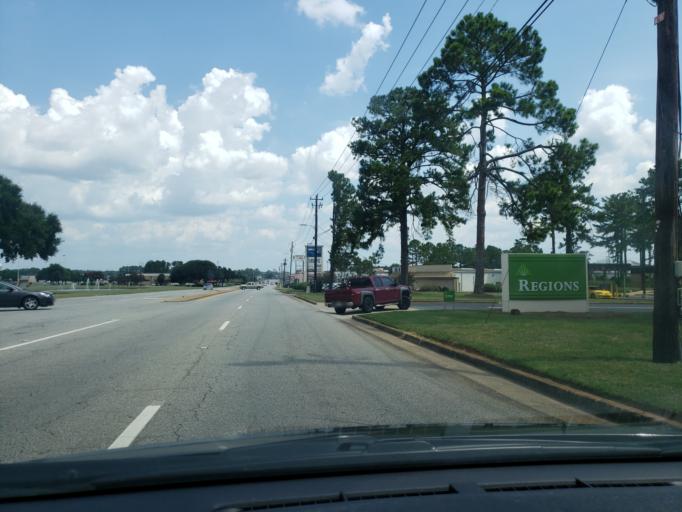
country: US
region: Georgia
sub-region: Dougherty County
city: Albany
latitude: 31.6163
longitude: -84.2201
